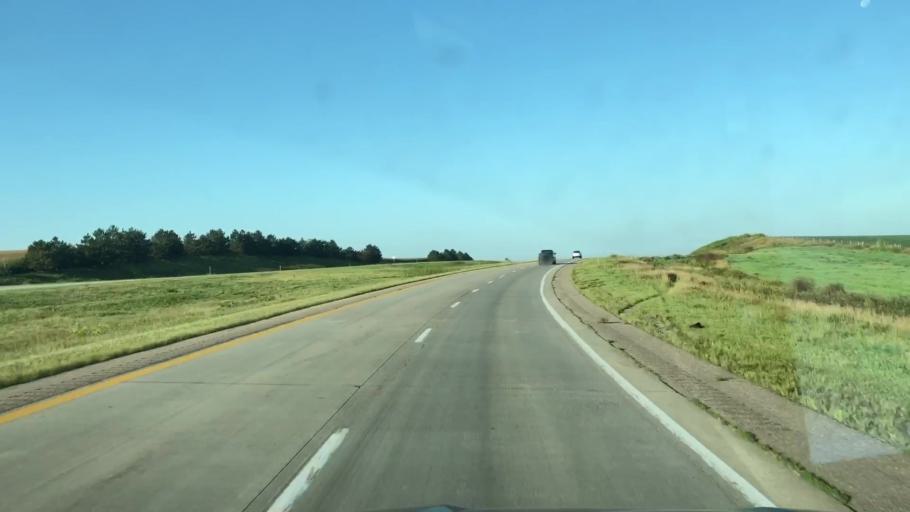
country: US
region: Iowa
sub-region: Sioux County
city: Alton
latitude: 43.0353
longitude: -95.9222
